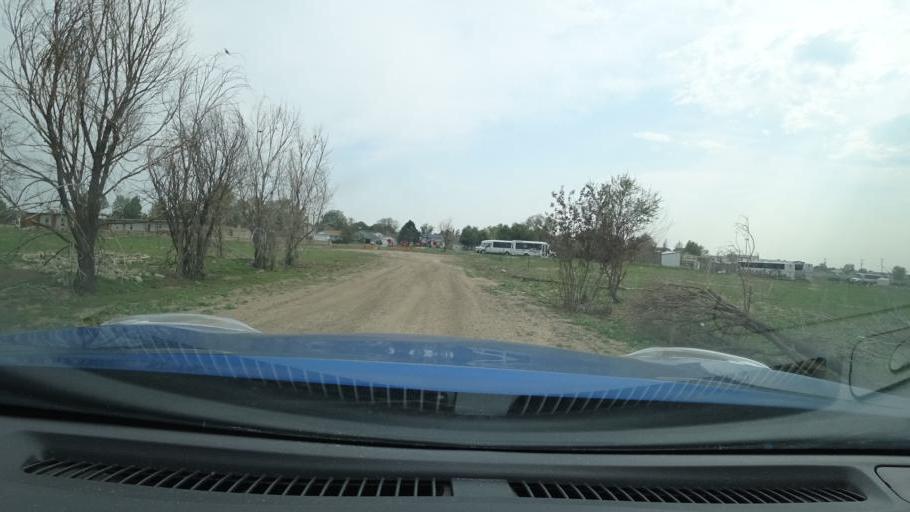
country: US
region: Colorado
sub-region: Adams County
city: Aurora
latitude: 39.7517
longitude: -104.7691
